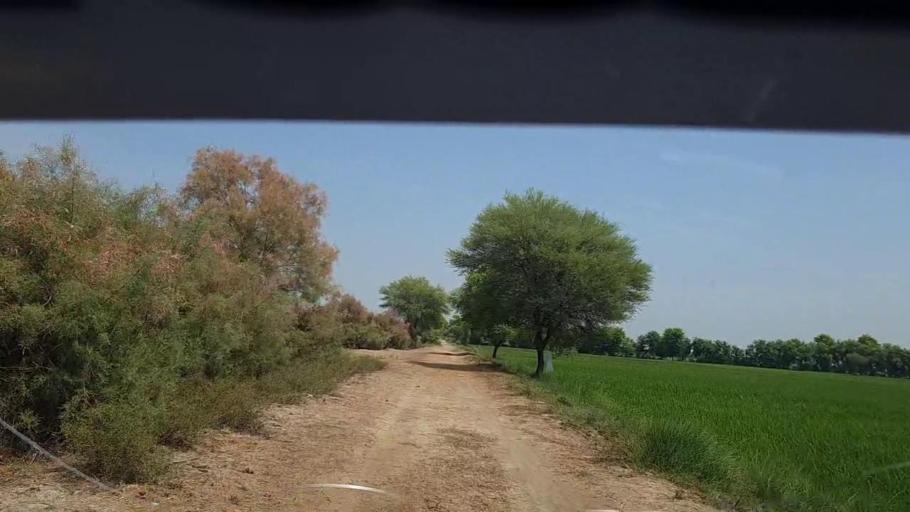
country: PK
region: Sindh
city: Tangwani
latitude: 28.2284
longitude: 68.9203
